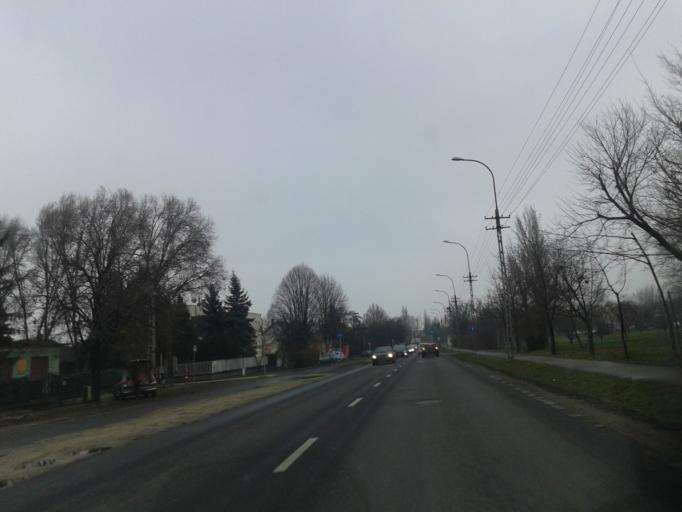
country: HU
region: Budapest
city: Budapest XXII. keruelet
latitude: 47.4081
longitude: 19.0547
